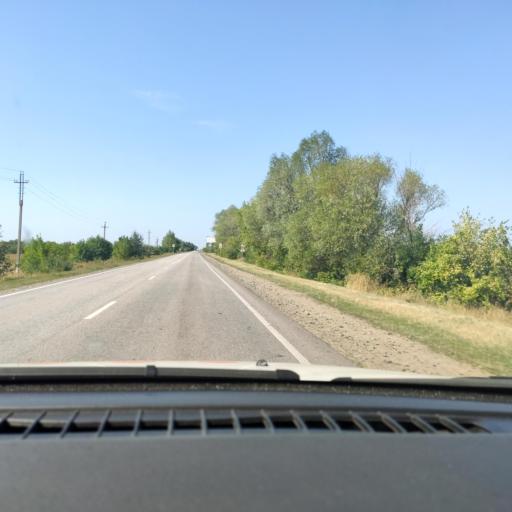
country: RU
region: Voronezj
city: Imeni Pervogo Maya
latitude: 50.7690
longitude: 39.3875
